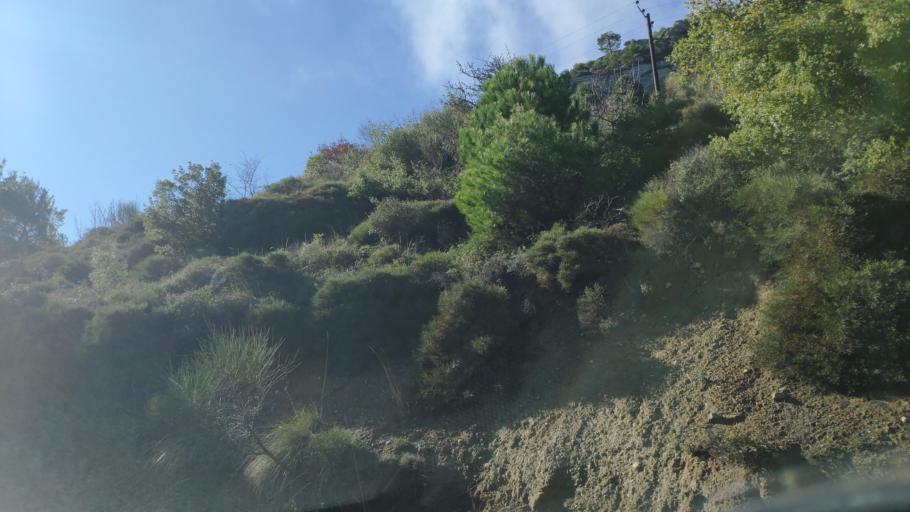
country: GR
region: West Greece
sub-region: Nomos Achaias
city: Aiyira
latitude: 38.0605
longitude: 22.4570
